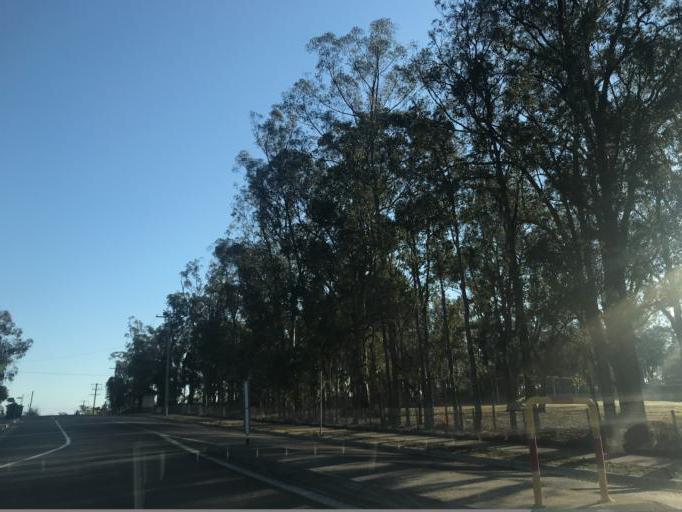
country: AU
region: New South Wales
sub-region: Cessnock
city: Cessnock
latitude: -32.9132
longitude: 151.3098
